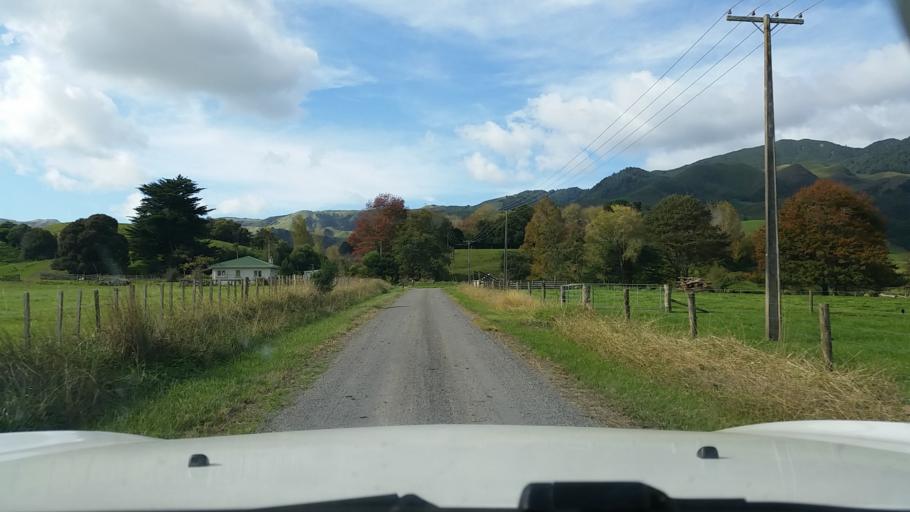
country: NZ
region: Waikato
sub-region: Hauraki District
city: Paeroa
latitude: -37.5104
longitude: 175.7001
